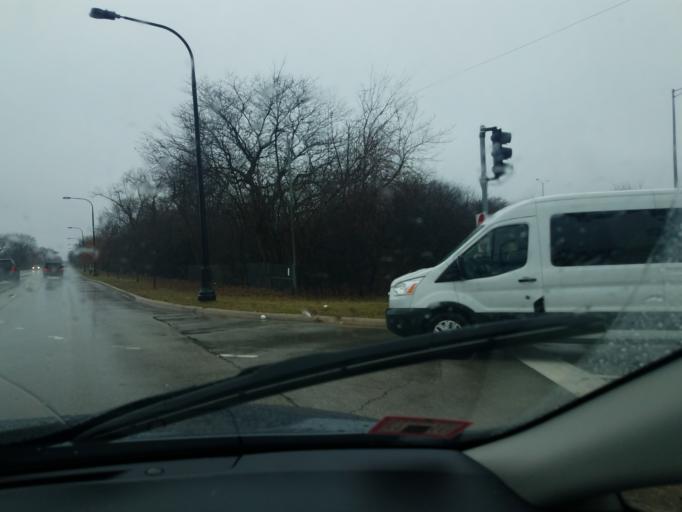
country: US
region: Illinois
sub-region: Cook County
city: Lincolnwood
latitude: 42.0099
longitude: -87.7481
